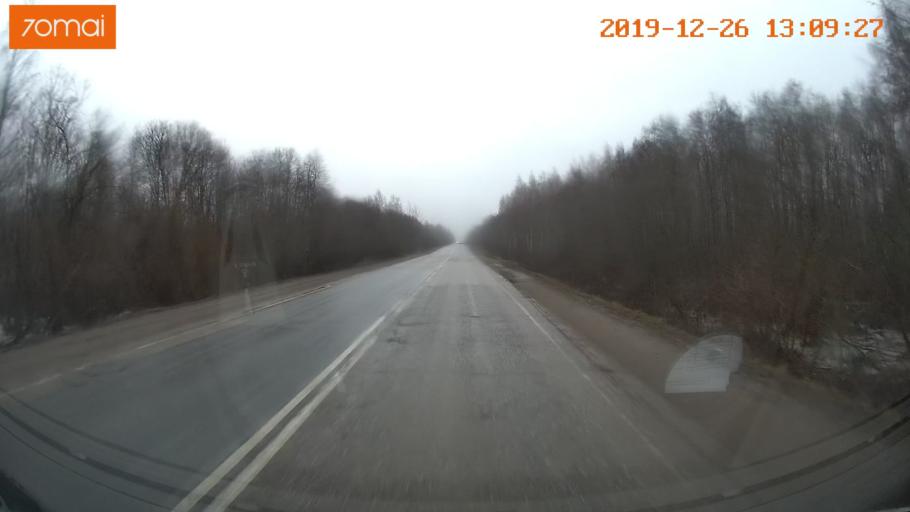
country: RU
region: Vologda
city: Cherepovets
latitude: 59.0469
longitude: 37.9581
